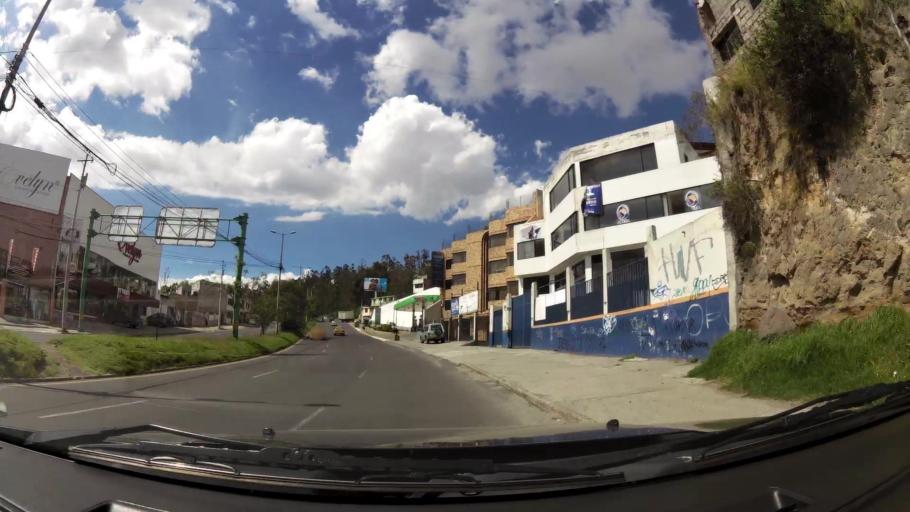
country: EC
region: Pichincha
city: Quito
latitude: -0.1026
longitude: -78.4873
